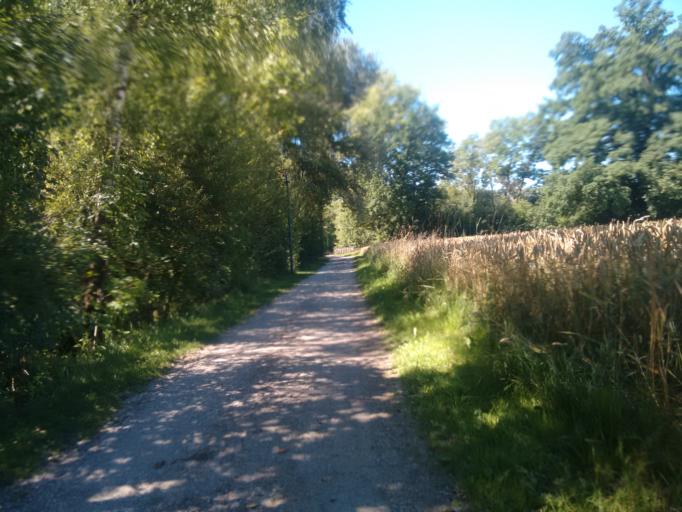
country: AT
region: Upper Austria
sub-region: Politischer Bezirk Grieskirchen
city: Bad Schallerbach
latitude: 48.2271
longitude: 13.9441
